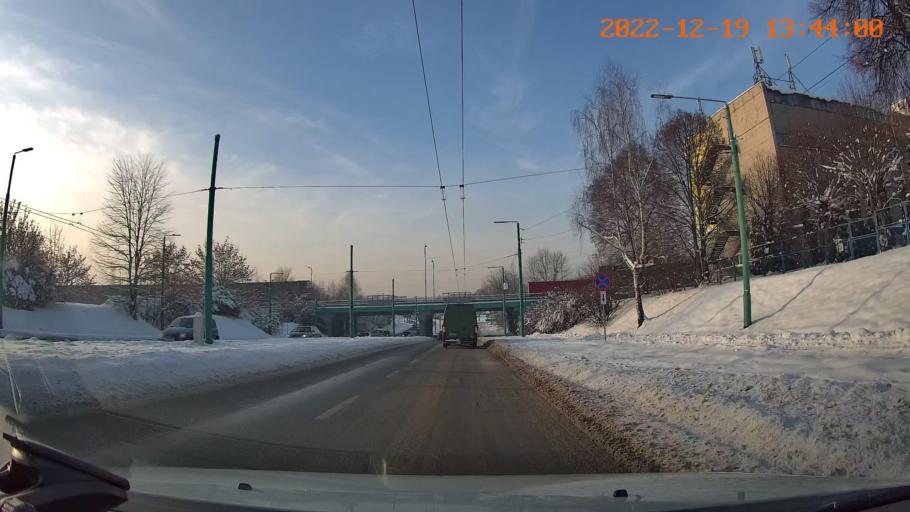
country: PL
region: Silesian Voivodeship
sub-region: Tychy
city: Cielmice
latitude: 50.1005
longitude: 19.0069
